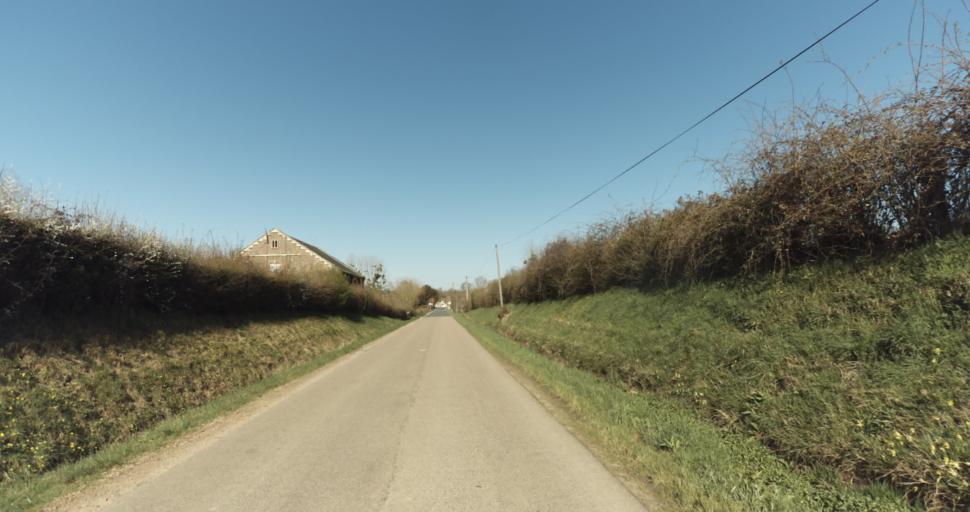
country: FR
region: Lower Normandy
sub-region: Departement du Calvados
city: Saint-Pierre-sur-Dives
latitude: 48.9733
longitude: 0.0423
